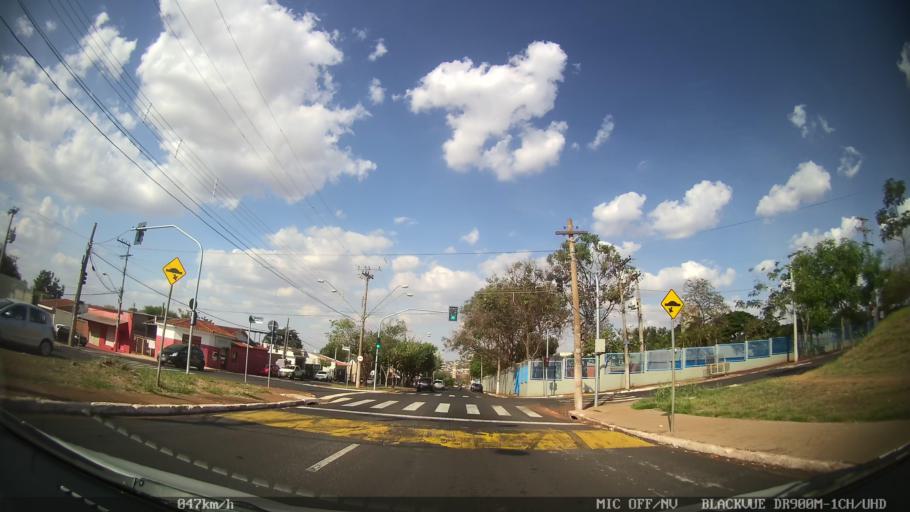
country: BR
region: Sao Paulo
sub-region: Ribeirao Preto
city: Ribeirao Preto
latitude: -21.1869
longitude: -47.8332
